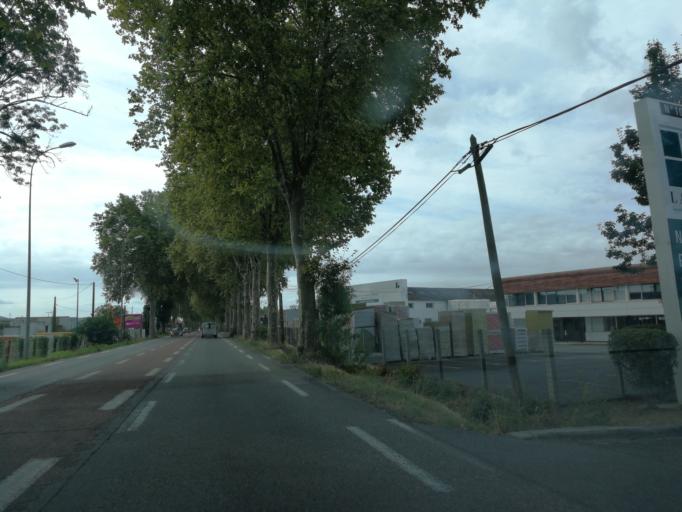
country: FR
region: Midi-Pyrenees
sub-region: Departement de la Haute-Garonne
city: Saint-Alban
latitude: 43.6825
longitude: 1.4067
